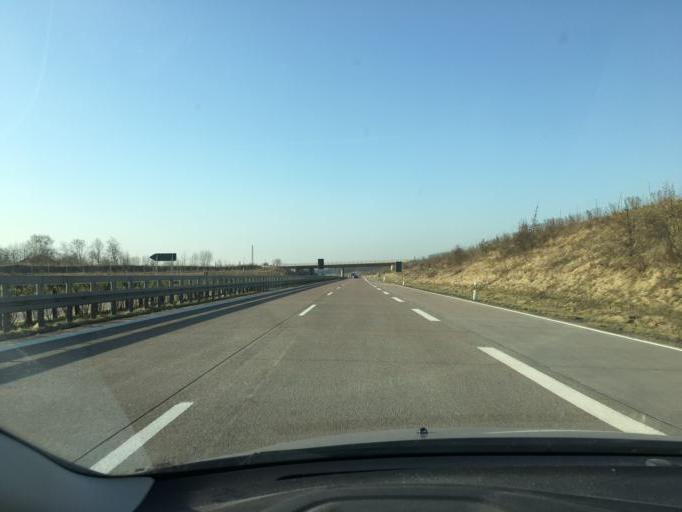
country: DE
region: Saxony
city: Penig
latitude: 50.9448
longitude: 12.6893
